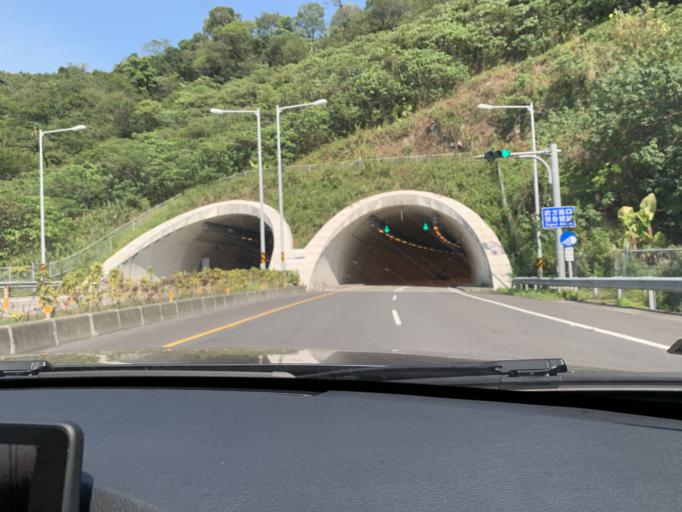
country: TW
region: Taiwan
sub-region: Yilan
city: Yilan
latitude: 24.5916
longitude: 121.8474
